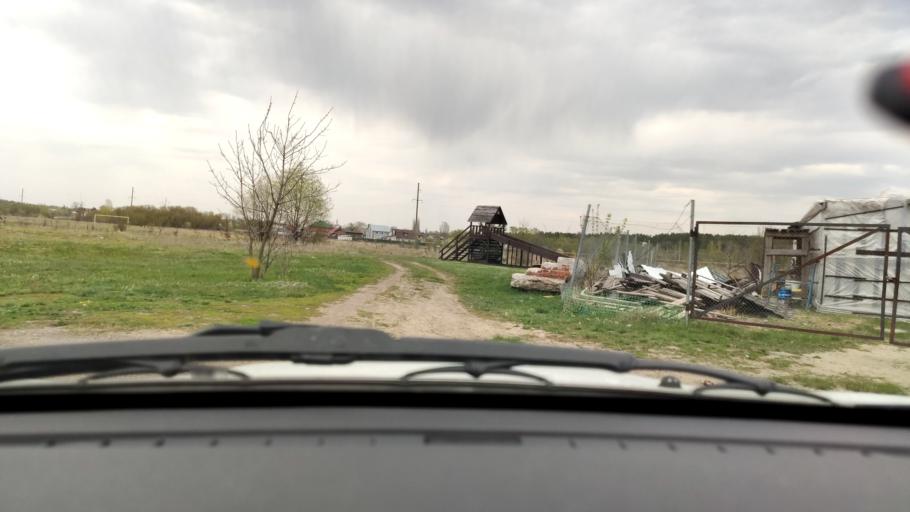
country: RU
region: Voronezj
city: Somovo
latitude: 51.7374
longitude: 39.3335
